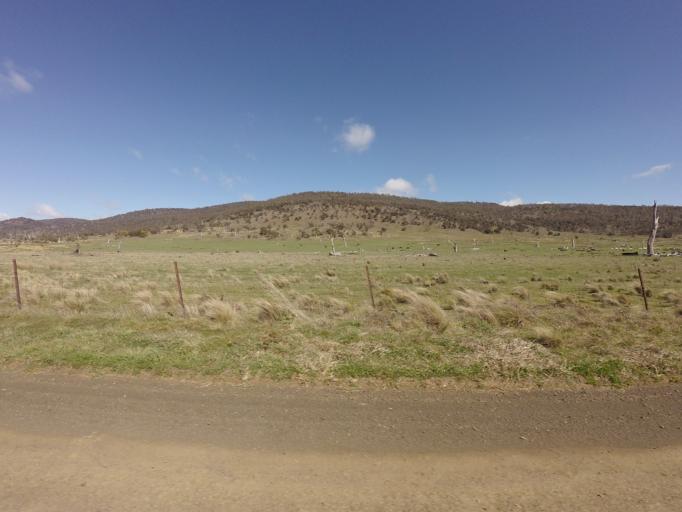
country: AU
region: Tasmania
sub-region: Northern Midlands
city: Evandale
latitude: -41.9275
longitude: 147.4120
